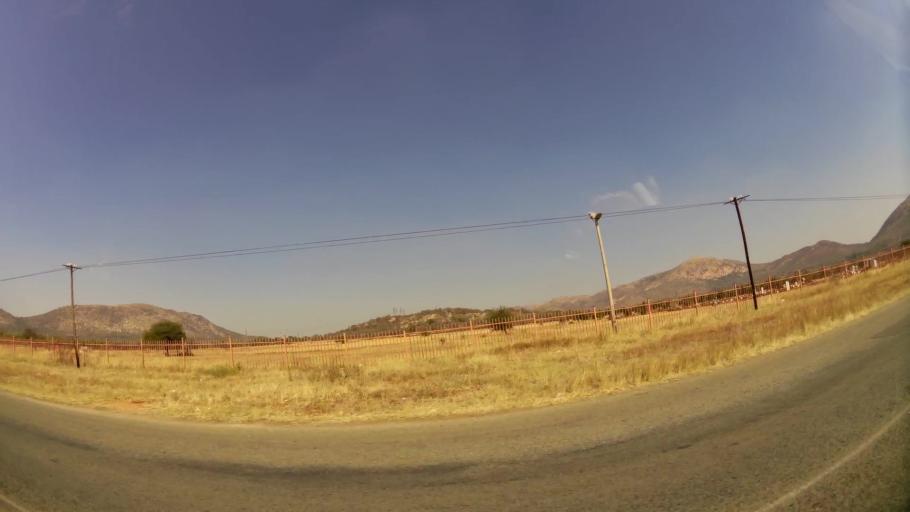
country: ZA
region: North-West
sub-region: Bojanala Platinum District Municipality
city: Rustenburg
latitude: -25.6336
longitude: 27.1678
